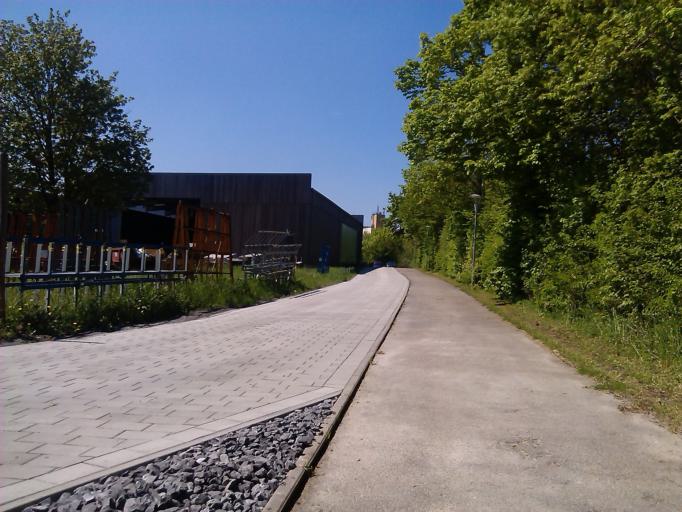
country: DE
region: Baden-Wuerttemberg
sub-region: Regierungsbezirk Stuttgart
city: Eppingen
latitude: 49.1371
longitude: 8.9246
